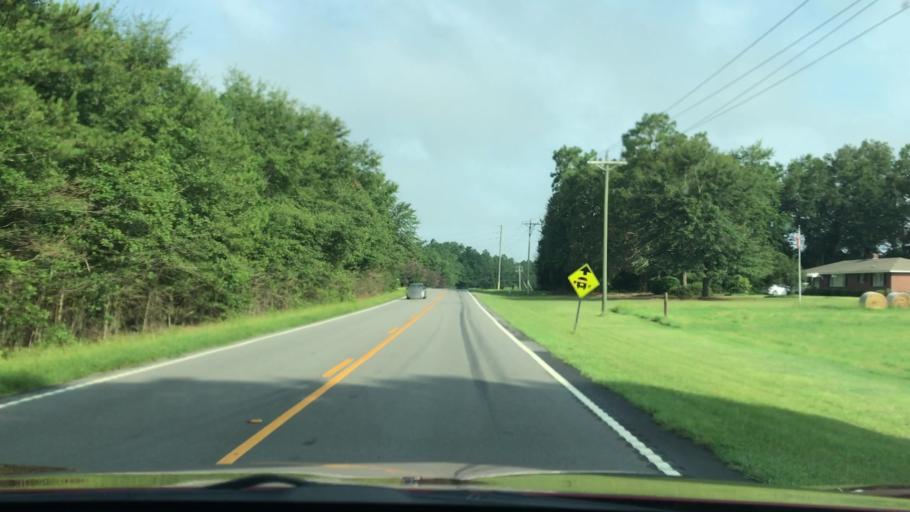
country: US
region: South Carolina
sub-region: Lexington County
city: Batesburg-Leesville
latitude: 33.7097
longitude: -81.4929
